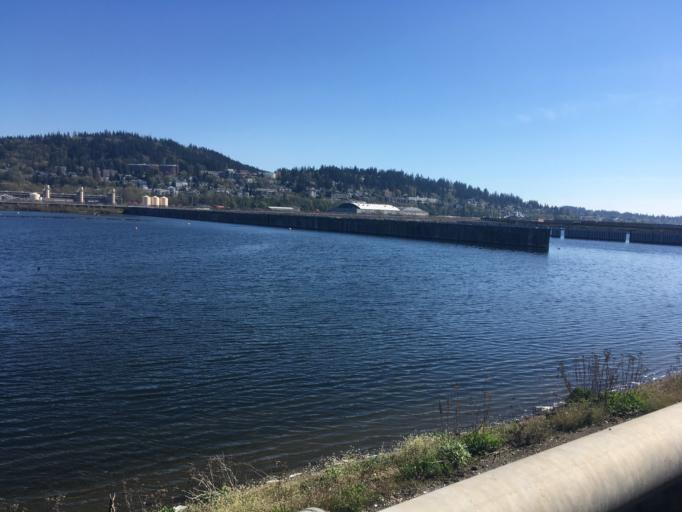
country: US
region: Washington
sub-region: Whatcom County
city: Bellingham
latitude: 48.7523
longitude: -122.4933
